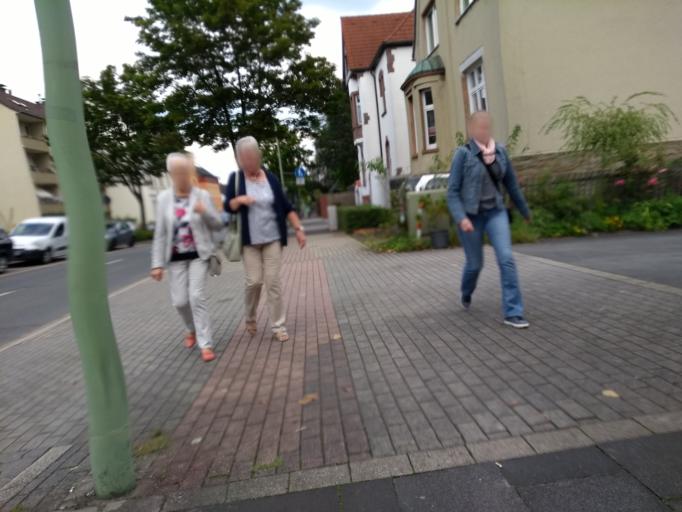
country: DE
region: North Rhine-Westphalia
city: Herdecke
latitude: 51.3933
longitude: 7.4674
